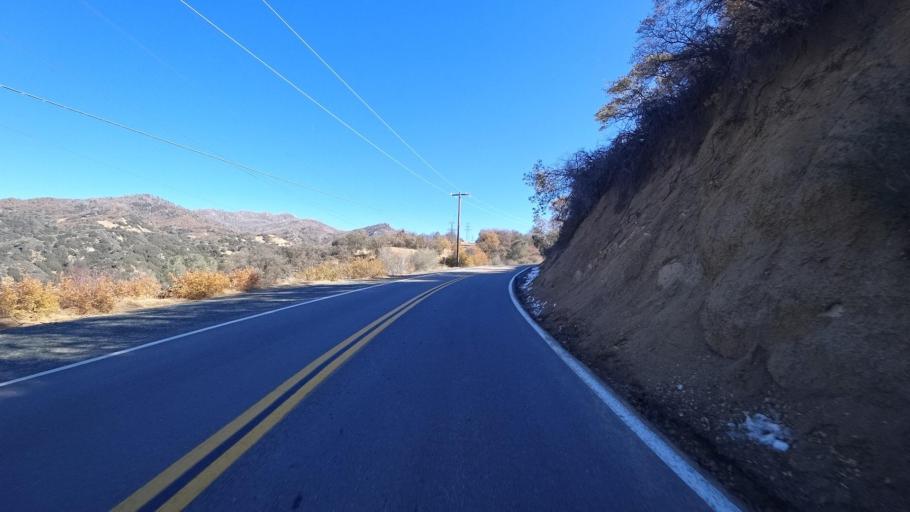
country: US
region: California
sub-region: Kern County
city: Alta Sierra
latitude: 35.7393
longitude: -118.6320
